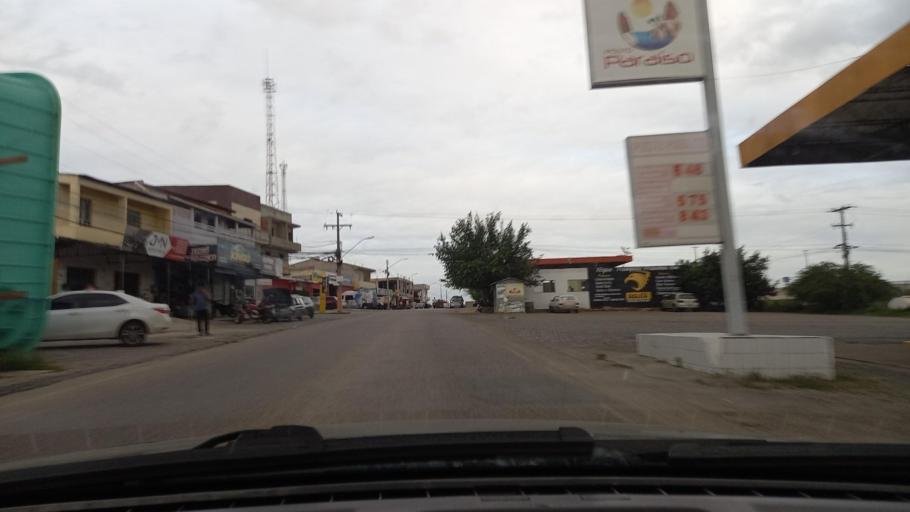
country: BR
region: Sergipe
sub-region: Caninde De Sao Francisco
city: Caninde de Sao Francisco
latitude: -9.6066
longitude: -37.7626
